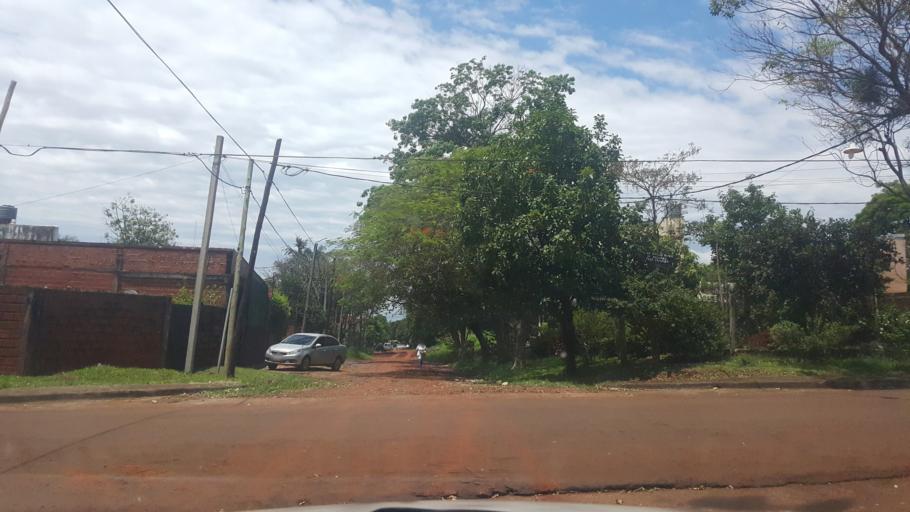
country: AR
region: Misiones
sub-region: Departamento de Capital
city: Posadas
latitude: -27.3870
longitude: -55.9147
